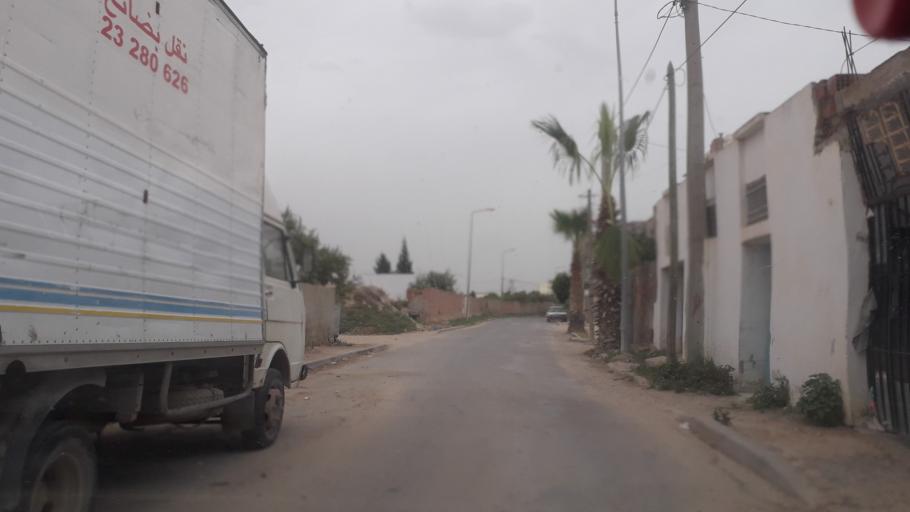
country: TN
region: Safaqis
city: Al Qarmadah
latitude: 34.7927
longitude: 10.7686
